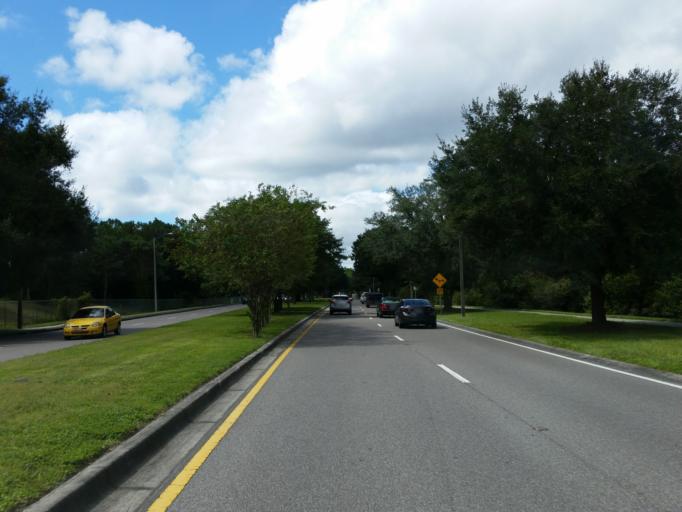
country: US
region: Florida
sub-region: Hillsborough County
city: Pebble Creek
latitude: 28.1423
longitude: -82.3412
